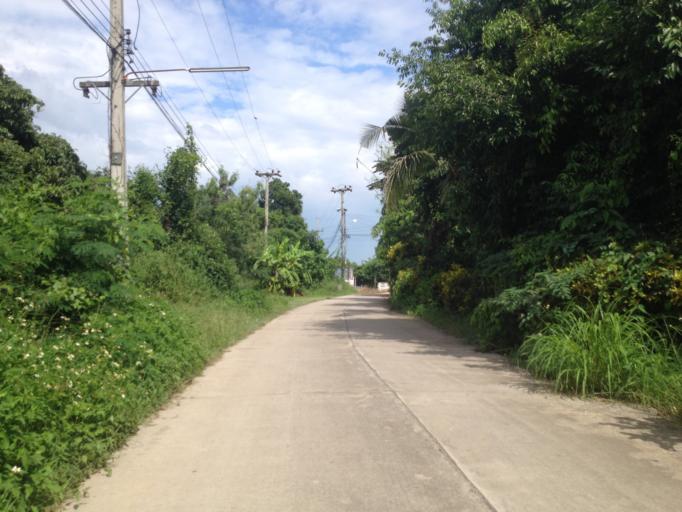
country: TH
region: Chiang Mai
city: Hang Dong
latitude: 18.6758
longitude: 98.8915
